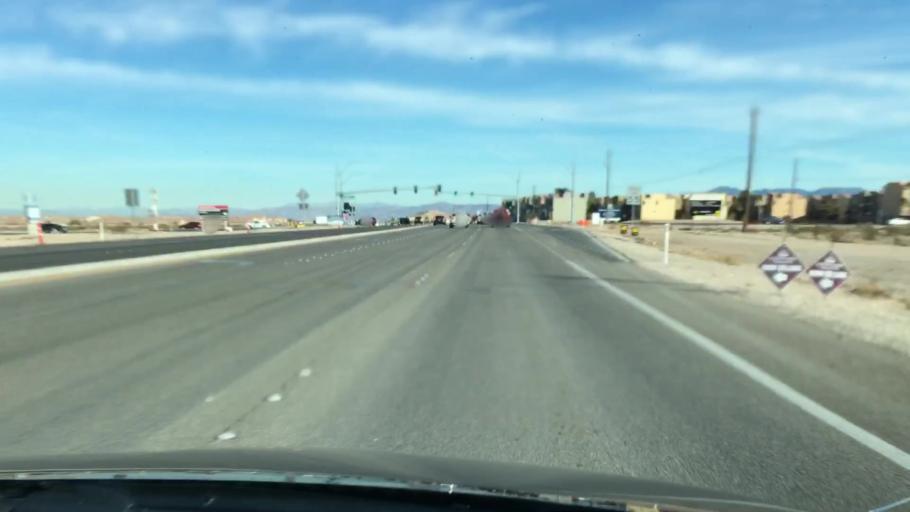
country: US
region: Nevada
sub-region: Clark County
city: Enterprise
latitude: 36.0206
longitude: -115.2998
